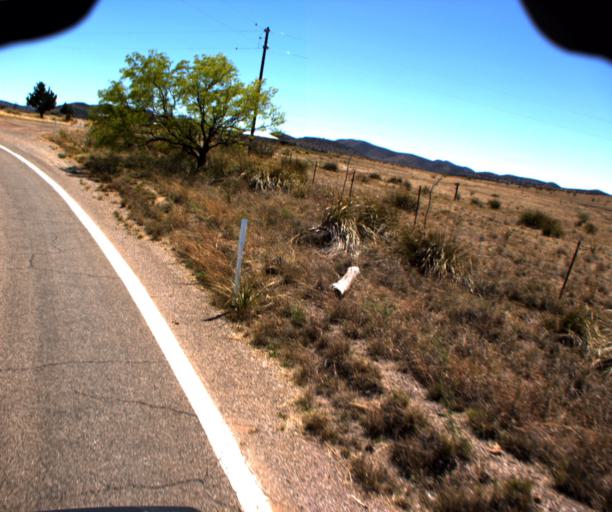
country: US
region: Arizona
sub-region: Cochise County
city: Huachuca City
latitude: 31.5862
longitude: -110.5630
